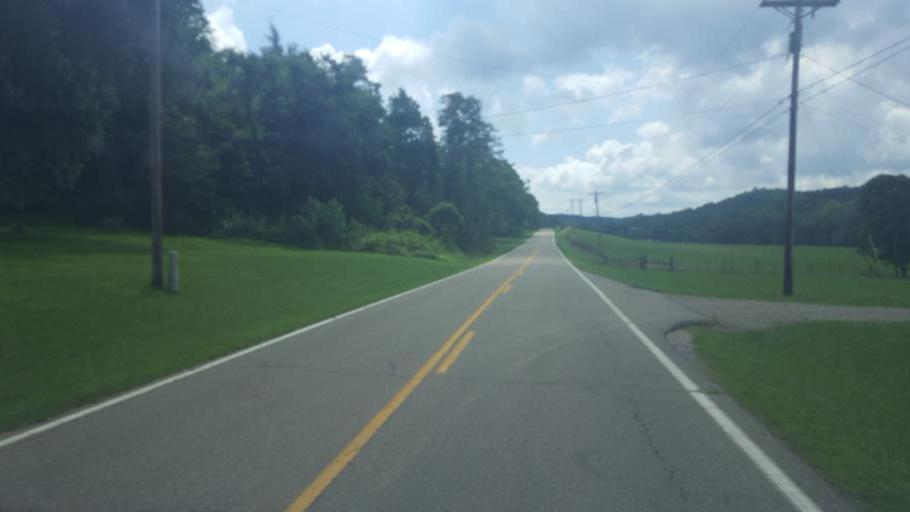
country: US
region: Ohio
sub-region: Ross County
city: Kingston
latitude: 39.4463
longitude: -82.7497
